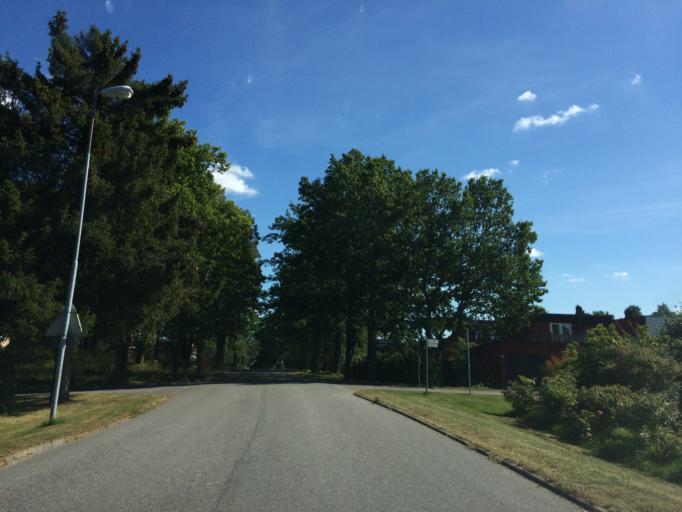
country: SE
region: Stockholm
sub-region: Upplands Vasby Kommun
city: Upplands Vaesby
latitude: 59.4622
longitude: 17.9050
